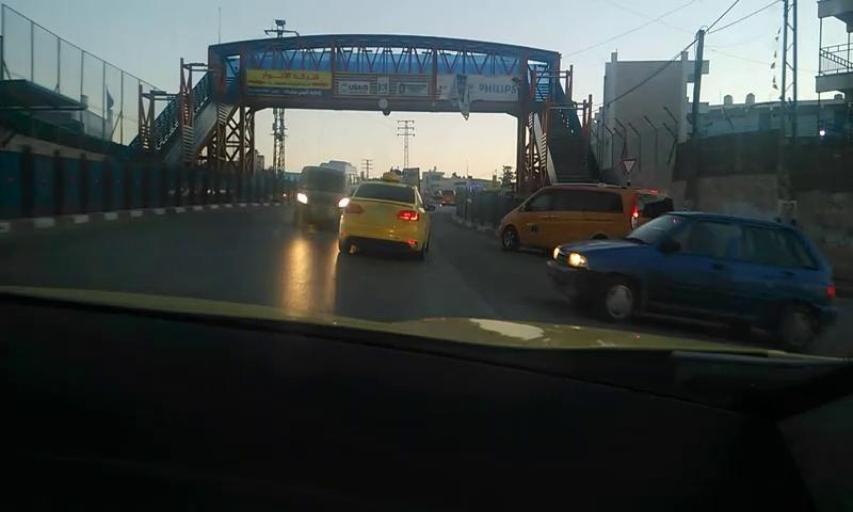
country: PS
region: West Bank
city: Surda
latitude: 31.9450
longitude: 35.2156
